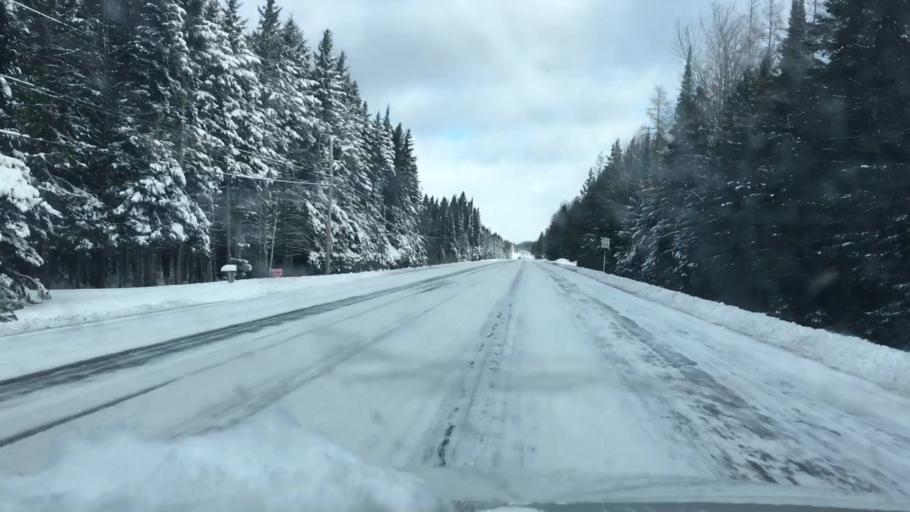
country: US
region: Maine
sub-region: Aroostook County
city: Madawaska
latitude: 47.0148
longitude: -68.0173
